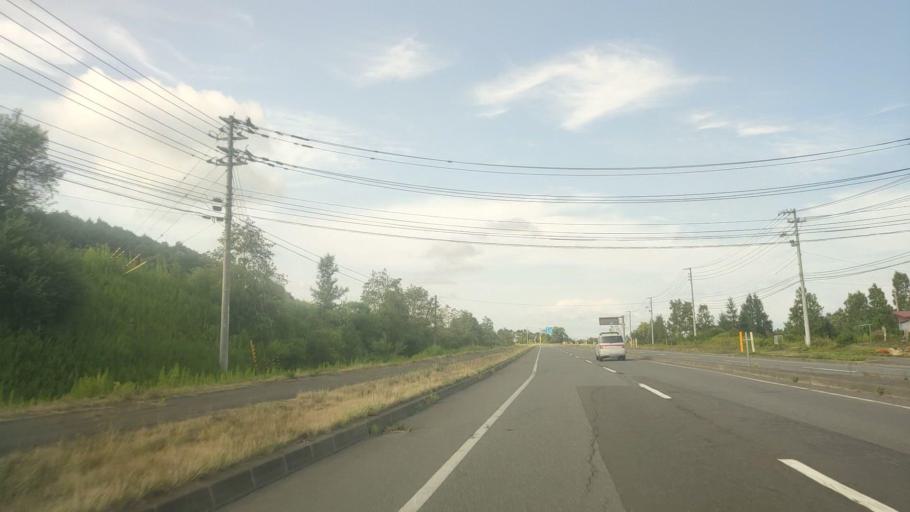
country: JP
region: Hokkaido
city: Chitose
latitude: 42.7728
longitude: 141.8259
